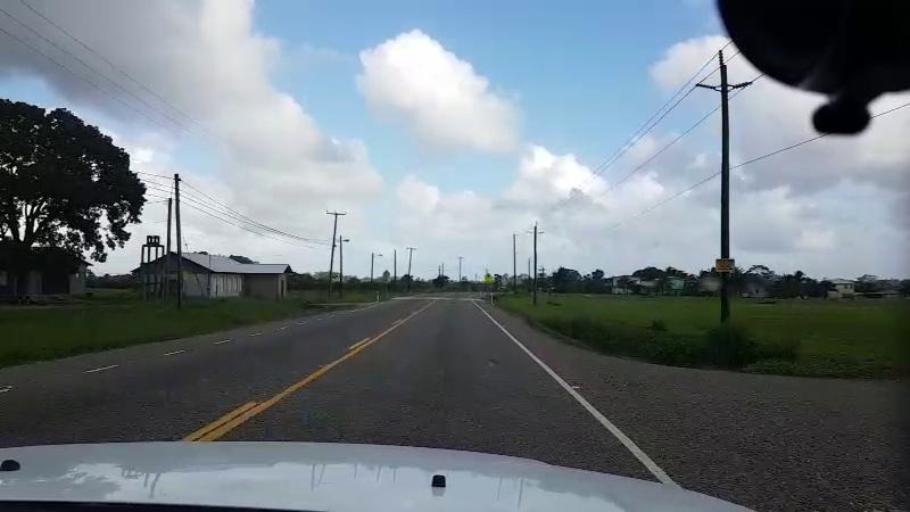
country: BZ
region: Stann Creek
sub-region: Dangriga
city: Dangriga
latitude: 16.9948
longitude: -88.3670
